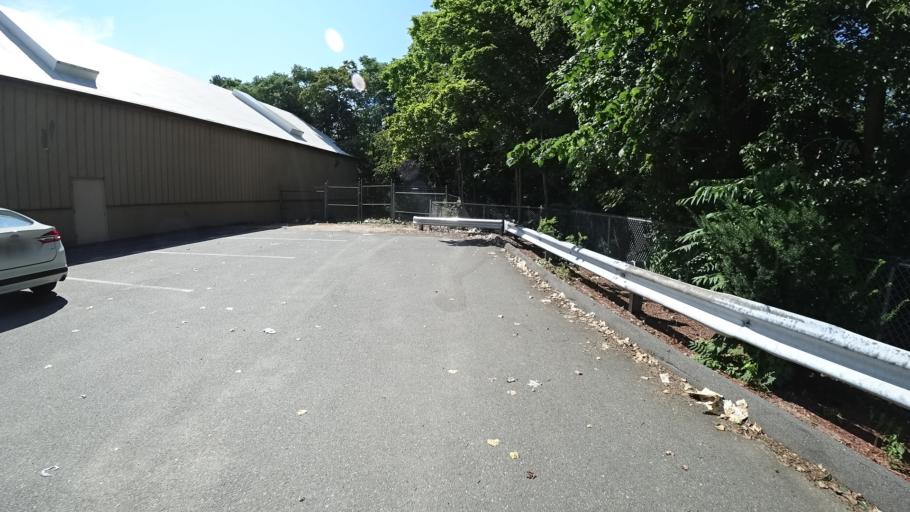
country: US
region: Massachusetts
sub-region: Norfolk County
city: Dedham
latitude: 42.2561
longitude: -71.1662
